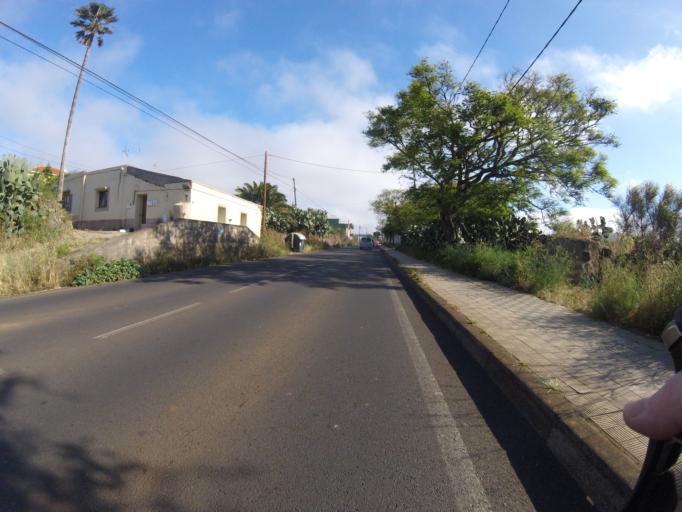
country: ES
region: Canary Islands
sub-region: Provincia de Santa Cruz de Tenerife
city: La Laguna
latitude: 28.4752
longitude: -16.3180
